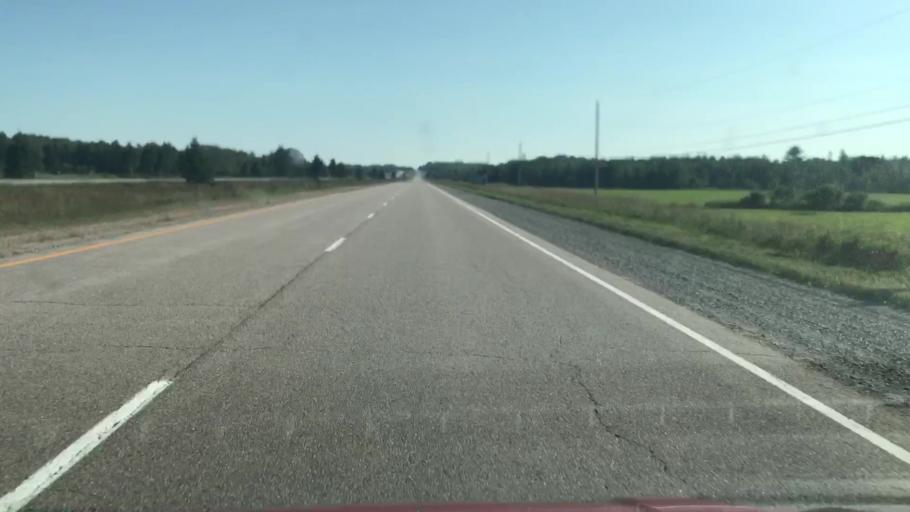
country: CA
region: Ontario
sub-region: Algoma
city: Sault Ste. Marie
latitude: 46.3671
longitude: -84.0679
